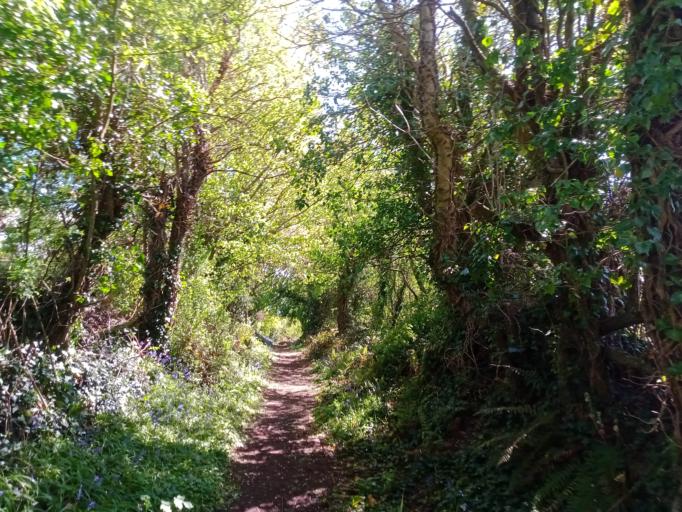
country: IE
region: Leinster
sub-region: Kilkenny
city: Kilkenny
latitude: 52.6915
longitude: -7.2637
